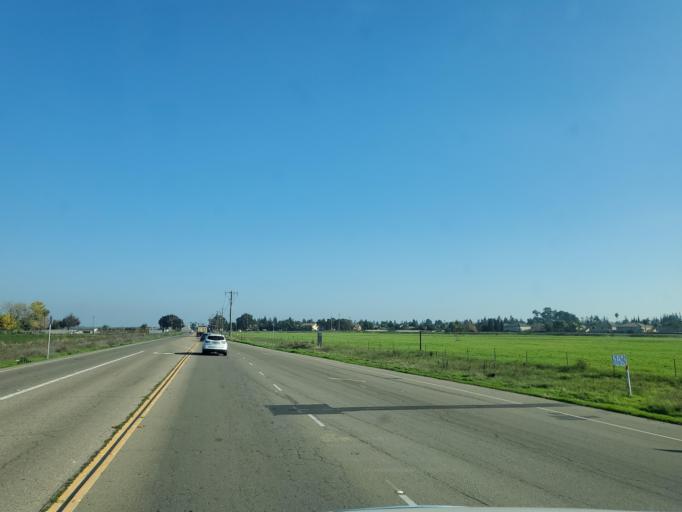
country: US
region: California
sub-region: San Joaquin County
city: Lincoln Village
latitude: 38.0576
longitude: -121.3382
